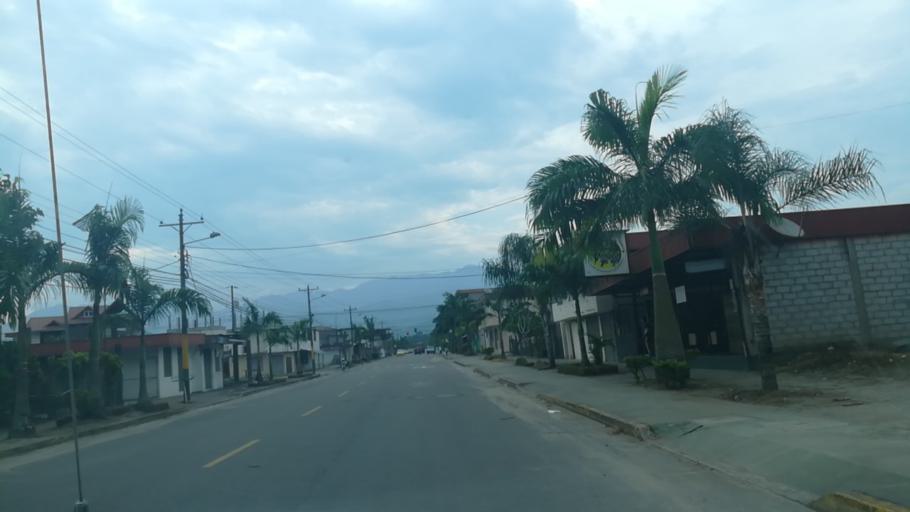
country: EC
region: Napo
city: Tena
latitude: -0.9855
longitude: -77.8177
